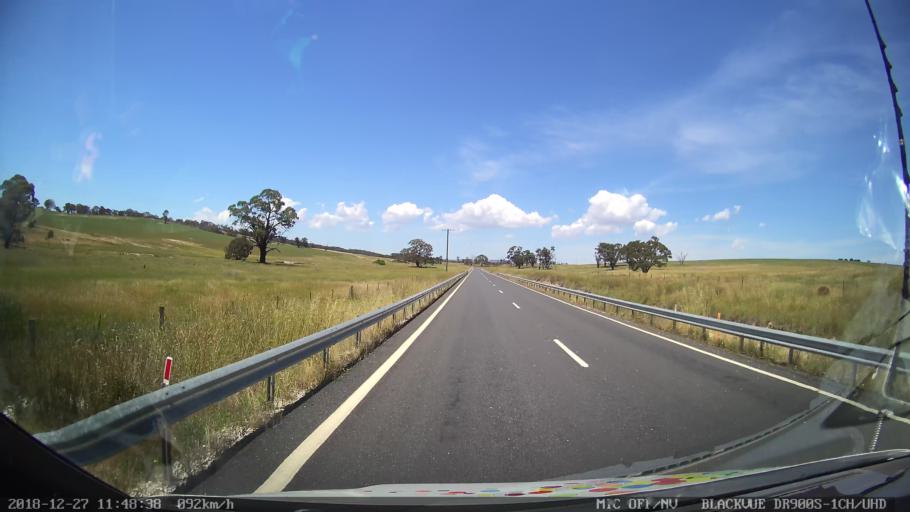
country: AU
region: New South Wales
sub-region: Bathurst Regional
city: Perthville
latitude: -33.6088
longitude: 149.4352
